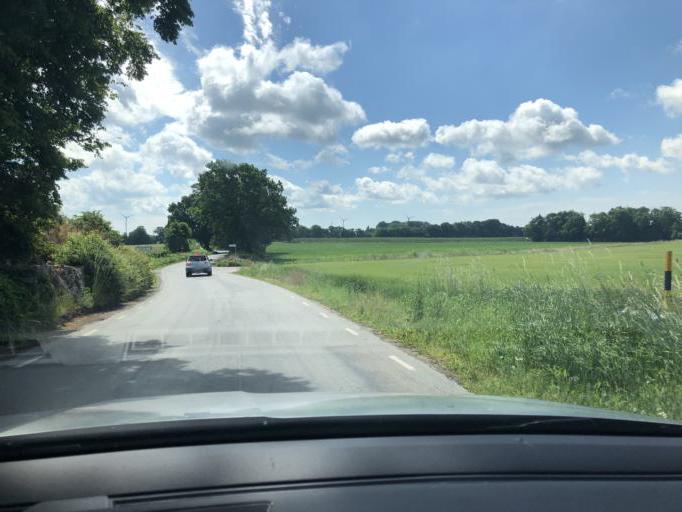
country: SE
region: Blekinge
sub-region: Solvesborgs Kommun
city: Soelvesborg
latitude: 56.0730
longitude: 14.6190
